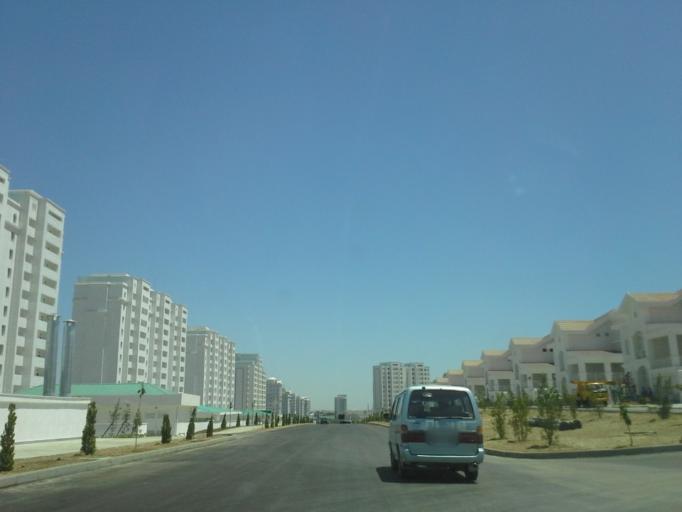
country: TM
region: Ahal
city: Ashgabat
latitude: 37.9386
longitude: 58.3561
